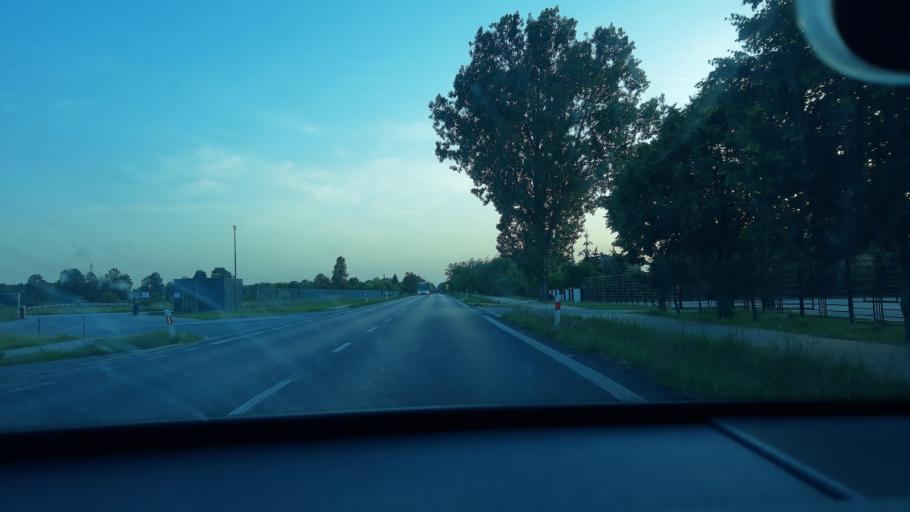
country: PL
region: Lodz Voivodeship
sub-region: Powiat zdunskowolski
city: Zapolice
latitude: 51.6056
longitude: 18.8556
